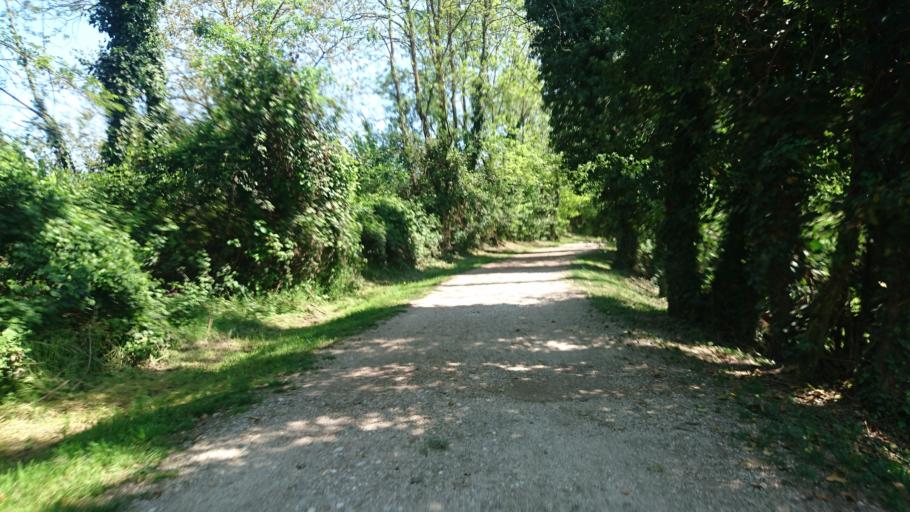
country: IT
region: Veneto
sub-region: Provincia di Treviso
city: Casier
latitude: 45.6466
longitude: 12.2735
